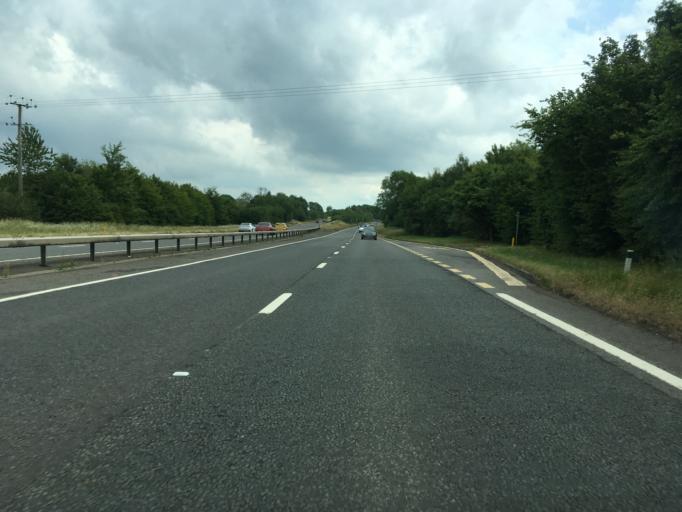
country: GB
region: England
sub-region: Gloucestershire
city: Coates
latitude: 51.7806
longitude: -2.0356
